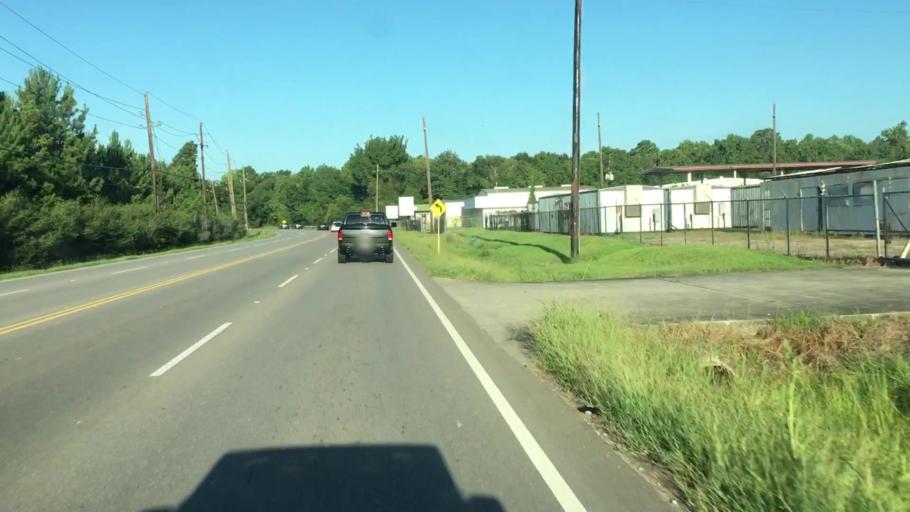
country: US
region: Texas
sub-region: Harris County
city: Humble
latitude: 29.9620
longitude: -95.2517
